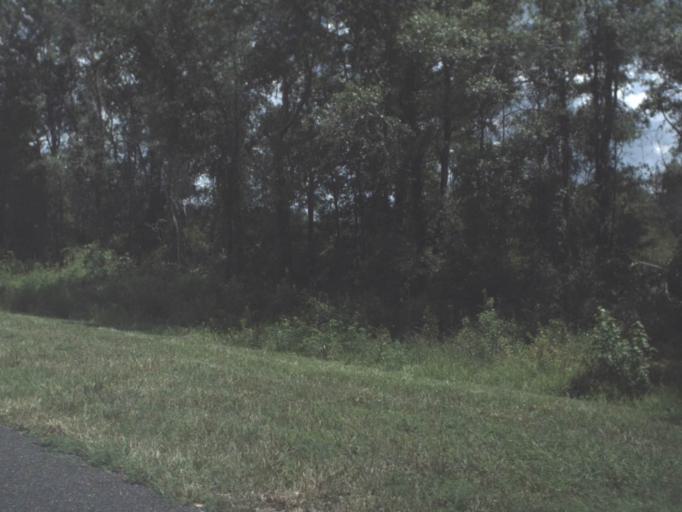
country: US
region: Florida
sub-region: Taylor County
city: Perry
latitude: 29.9743
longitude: -83.4836
